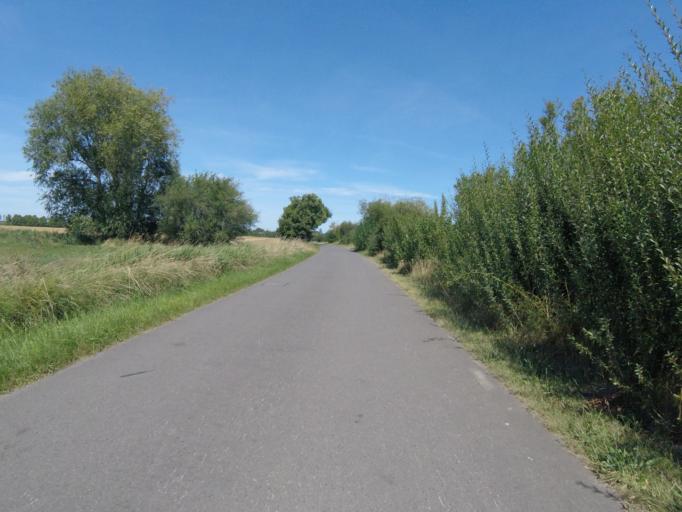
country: DE
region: Brandenburg
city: Mittenwalde
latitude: 52.2779
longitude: 13.5428
